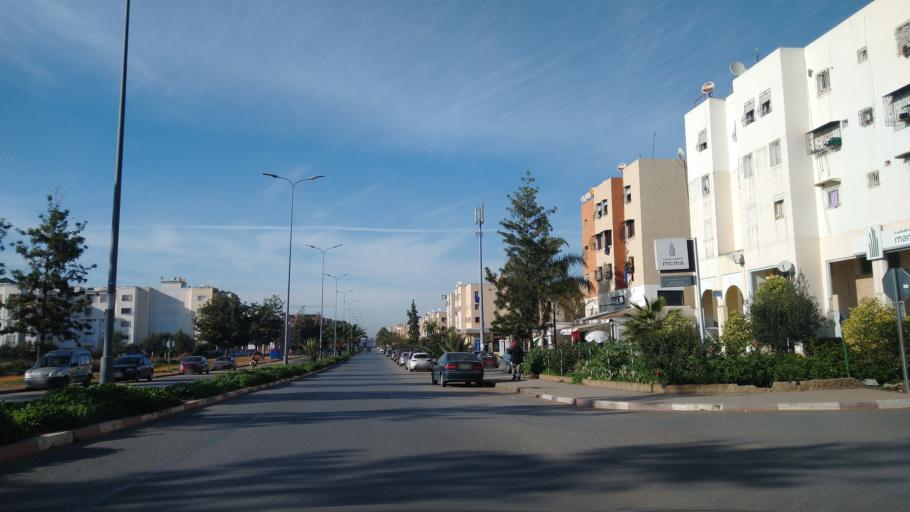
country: MA
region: Rabat-Sale-Zemmour-Zaer
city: Sale
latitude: 33.9924
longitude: -6.7430
